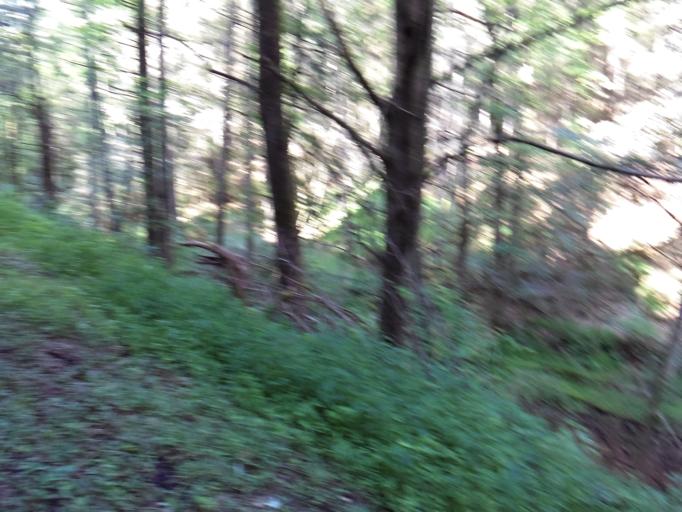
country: US
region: Virginia
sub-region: Washington County
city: Abingdon
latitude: 36.6906
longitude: -81.9395
